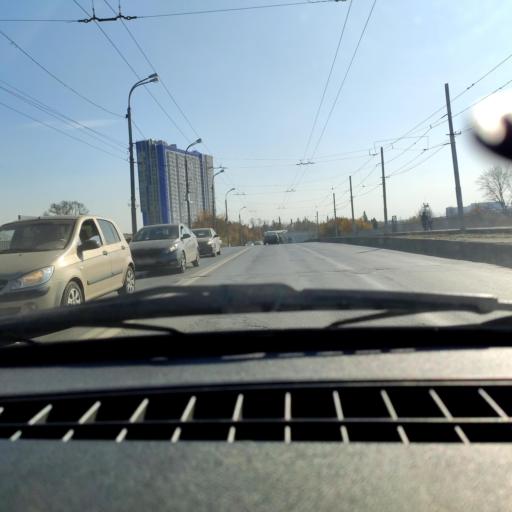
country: RU
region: Bashkortostan
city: Ufa
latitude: 54.8013
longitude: 56.1378
